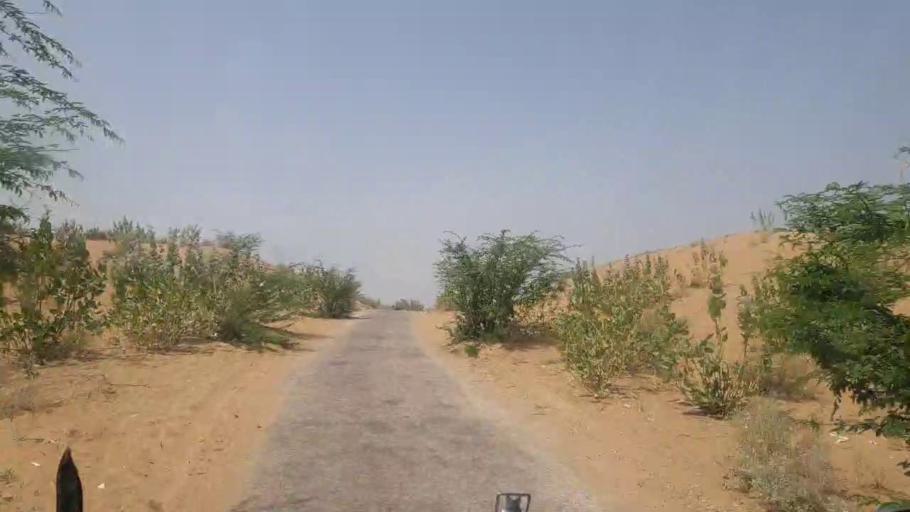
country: PK
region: Sindh
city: Islamkot
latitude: 25.1335
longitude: 70.2112
